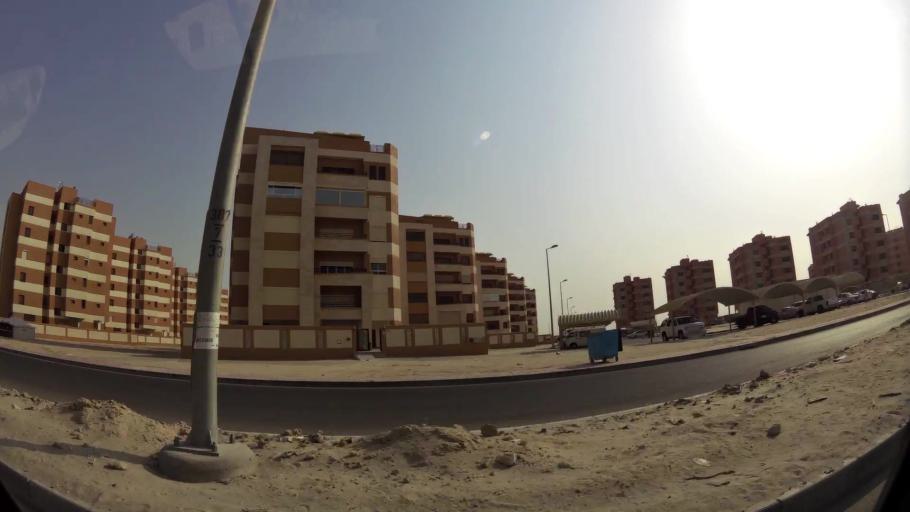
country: KW
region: Al Asimah
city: Ar Rabiyah
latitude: 29.3312
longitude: 47.8131
